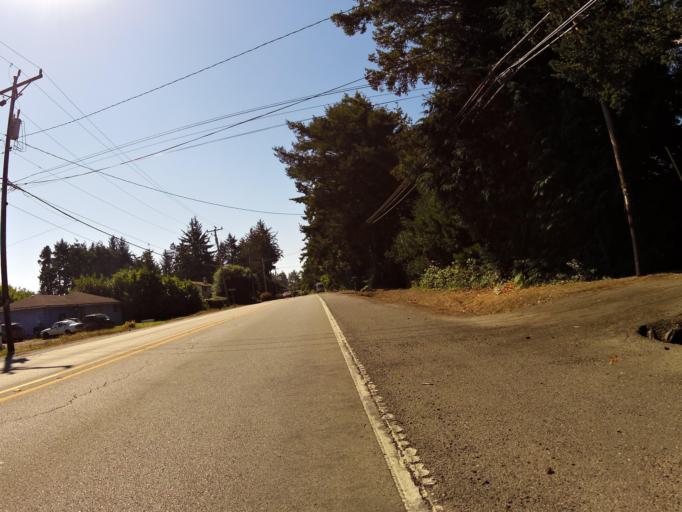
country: US
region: Oregon
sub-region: Coos County
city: Barview
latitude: 43.3539
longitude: -124.3123
